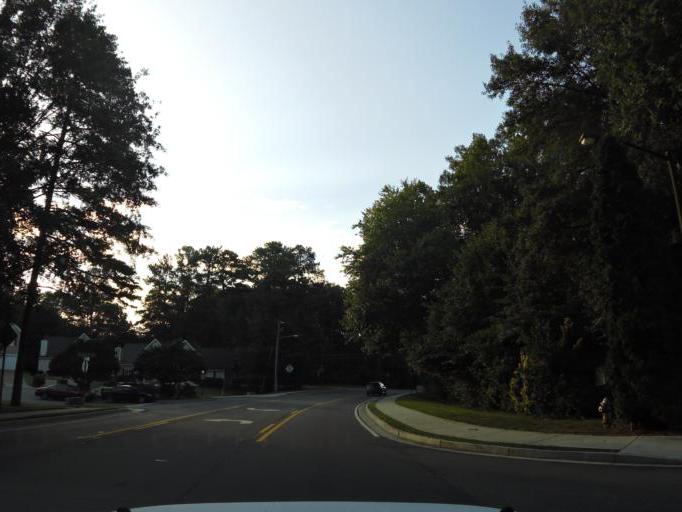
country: US
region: Georgia
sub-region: Cobb County
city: Kennesaw
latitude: 34.0270
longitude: -84.6257
